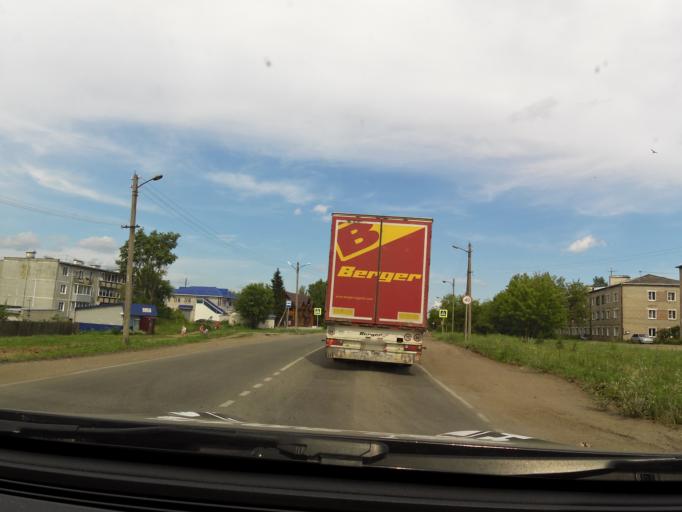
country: RU
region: Kirov
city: Stulovo
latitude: 58.7187
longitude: 50.1345
